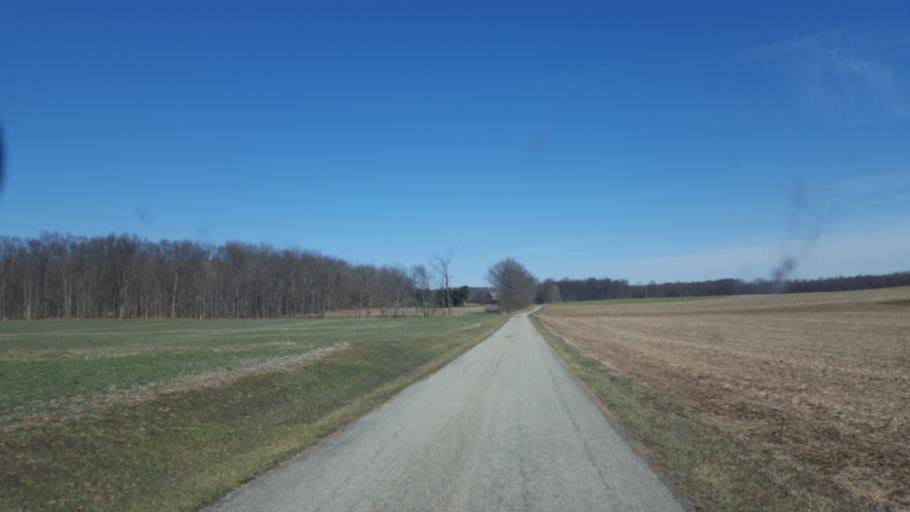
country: US
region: Ohio
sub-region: Knox County
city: Fredericktown
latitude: 40.5176
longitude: -82.5680
